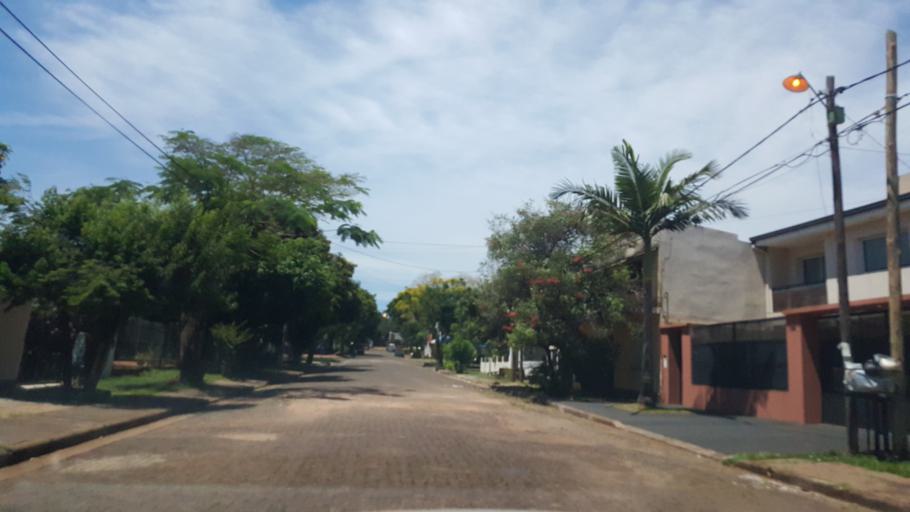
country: AR
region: Misiones
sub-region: Departamento de Capital
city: Posadas
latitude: -27.3962
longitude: -55.8994
